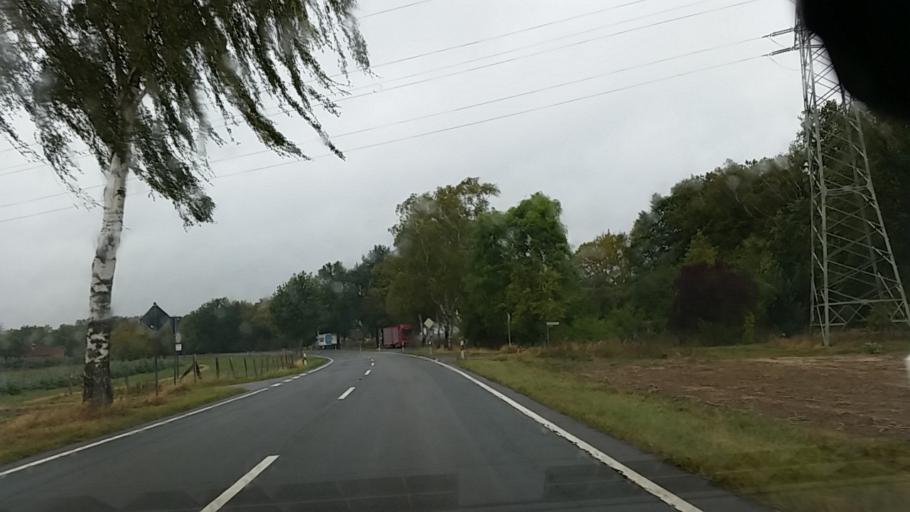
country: DE
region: Lower Saxony
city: Wieren
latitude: 52.8971
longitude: 10.6507
